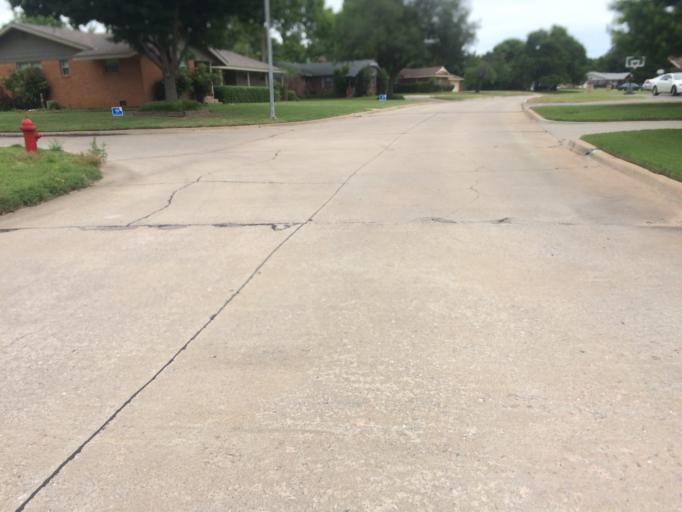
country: US
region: Oklahoma
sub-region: Cleveland County
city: Norman
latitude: 35.2123
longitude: -97.4786
